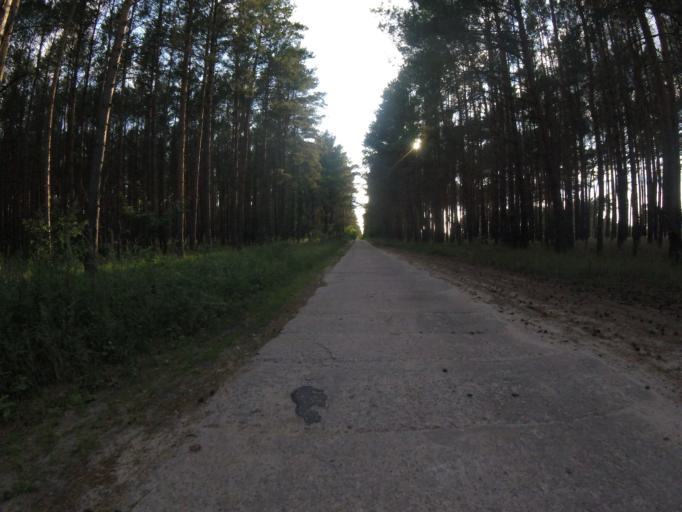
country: DE
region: Brandenburg
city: Schwerin
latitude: 52.1971
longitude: 13.6062
